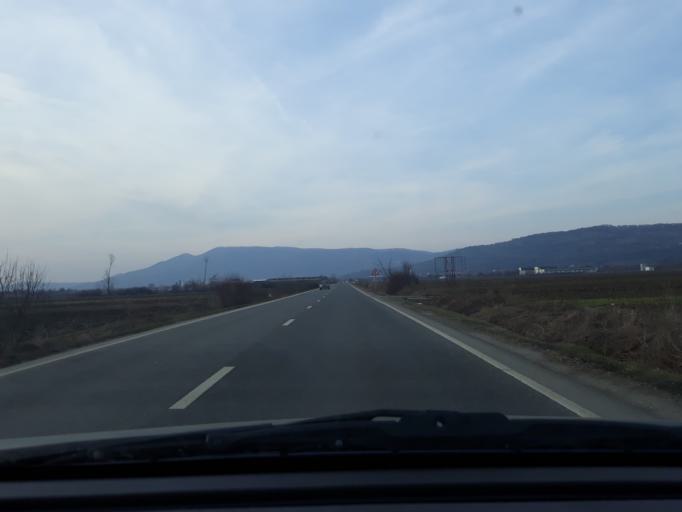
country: RO
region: Salaj
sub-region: Comuna Periceiu
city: Periceiu
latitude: 47.2189
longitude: 22.8892
